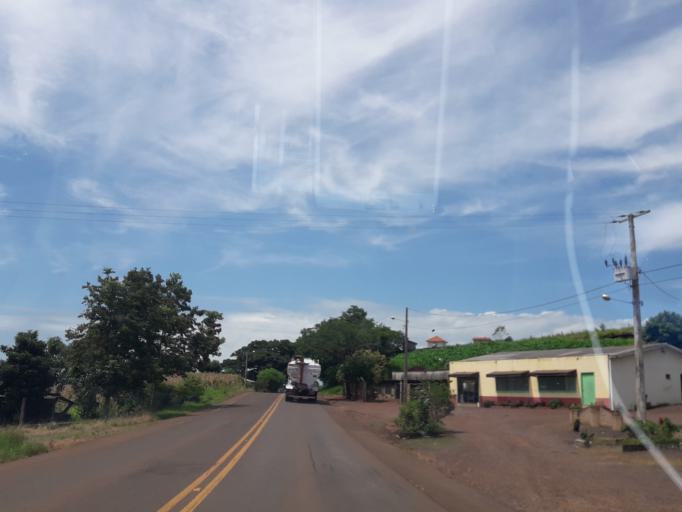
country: BR
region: Rio Grande do Sul
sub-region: Frederico Westphalen
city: Frederico Westphalen
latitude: -26.8581
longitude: -53.4960
